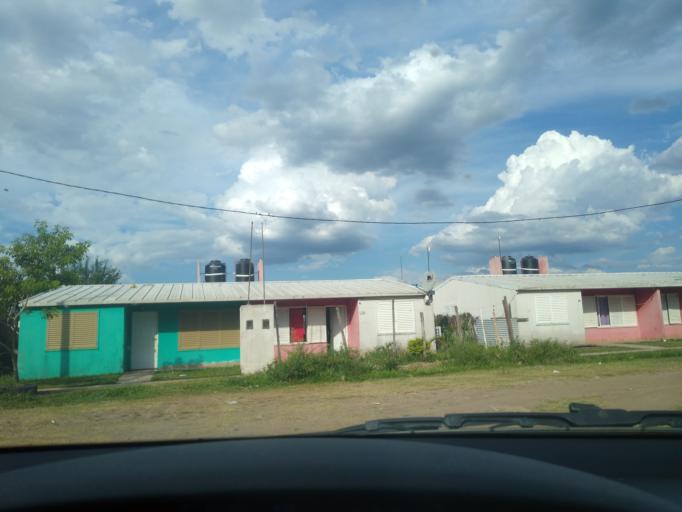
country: AR
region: Chaco
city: Fontana
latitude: -27.4047
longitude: -59.0475
